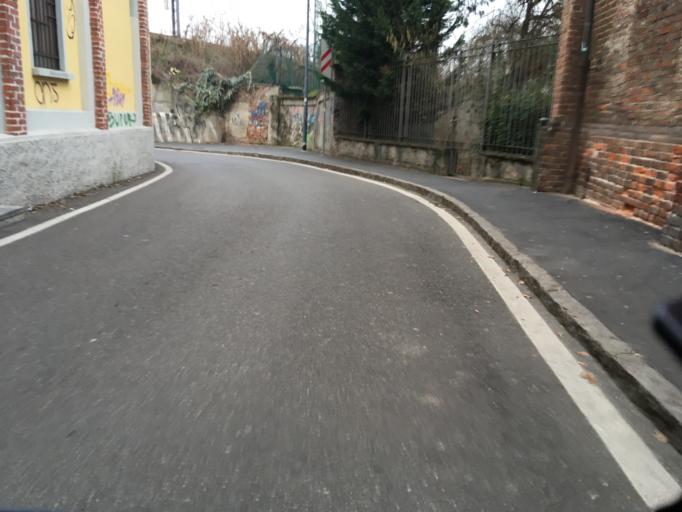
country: IT
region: Lombardy
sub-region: Citta metropolitana di Milano
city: Romano Banco
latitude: 45.4479
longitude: 9.1547
